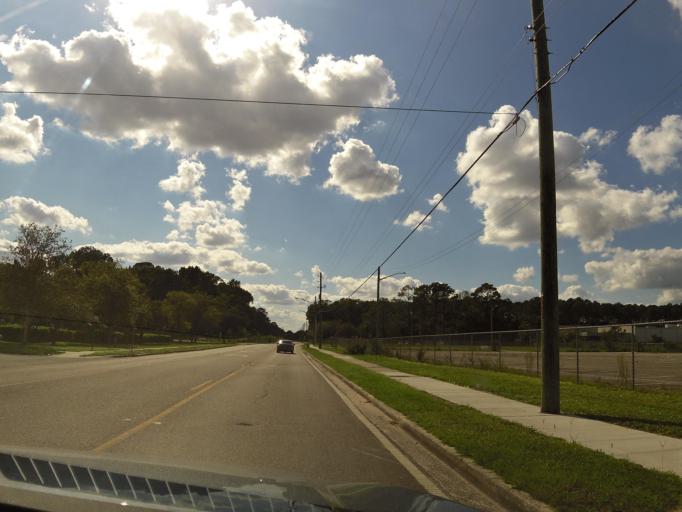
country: US
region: Florida
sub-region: Duval County
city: Jacksonville
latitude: 30.3439
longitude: -81.7255
